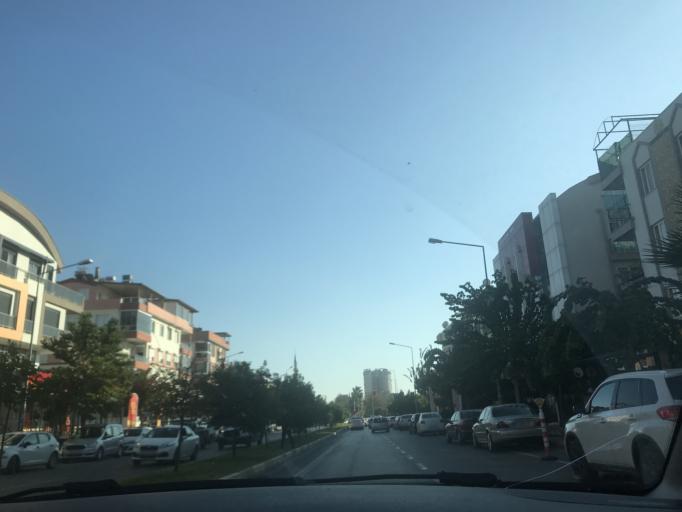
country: TR
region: Antalya
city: Antalya
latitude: 36.8850
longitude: 30.6478
